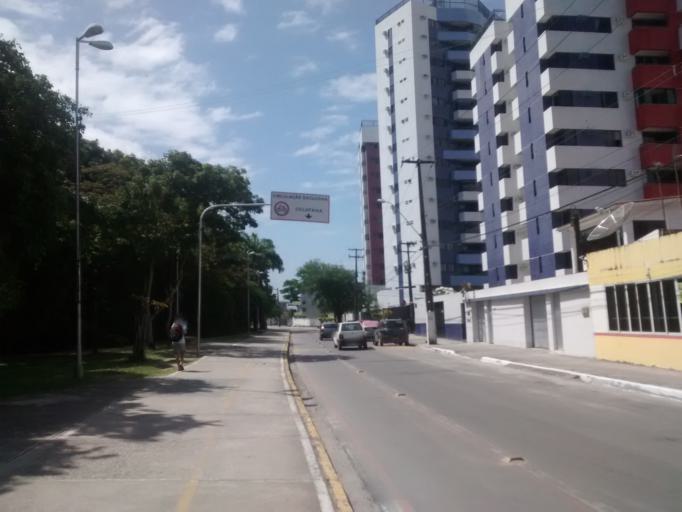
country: BR
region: Pernambuco
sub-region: Recife
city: Recife
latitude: -8.0943
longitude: -34.9134
